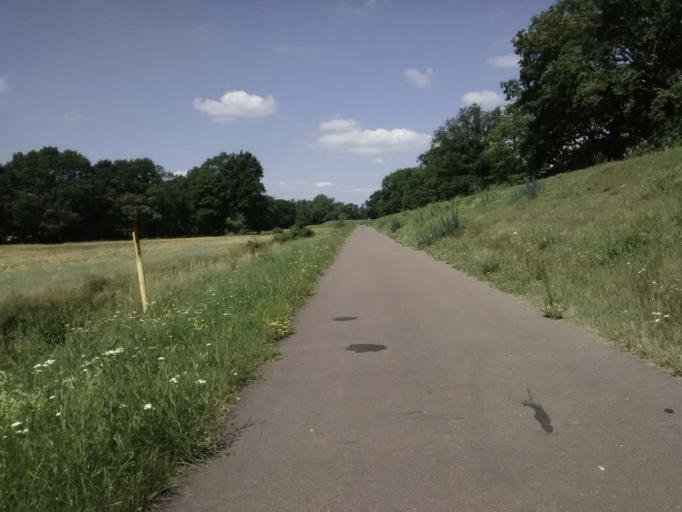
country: DE
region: Saxony-Anhalt
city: Worlitz
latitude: 51.8433
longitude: 12.4482
